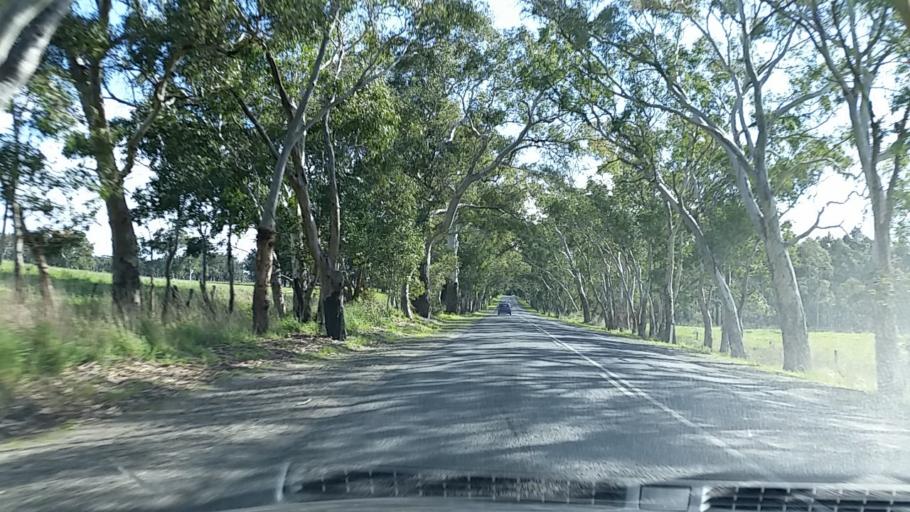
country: AU
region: South Australia
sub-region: Alexandrina
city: Mount Compass
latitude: -35.2642
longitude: 138.6492
